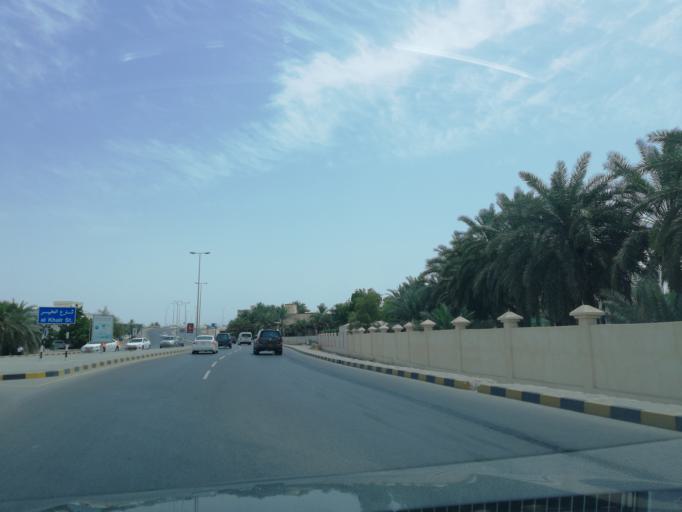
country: OM
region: Muhafazat Masqat
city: As Sib al Jadidah
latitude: 23.6789
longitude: 58.1382
